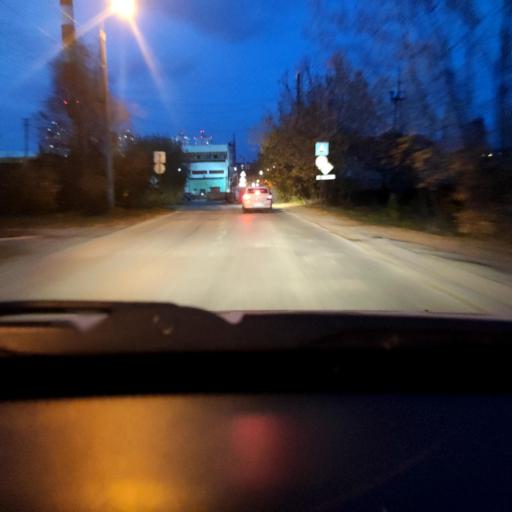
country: RU
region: Perm
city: Perm
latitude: 57.9970
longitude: 56.3148
